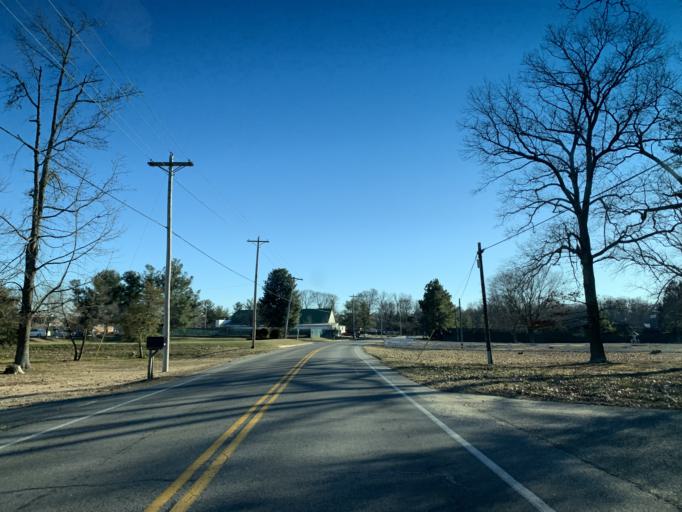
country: US
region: Maryland
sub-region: Saint Mary's County
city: Charlotte Hall
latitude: 38.4980
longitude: -76.7769
